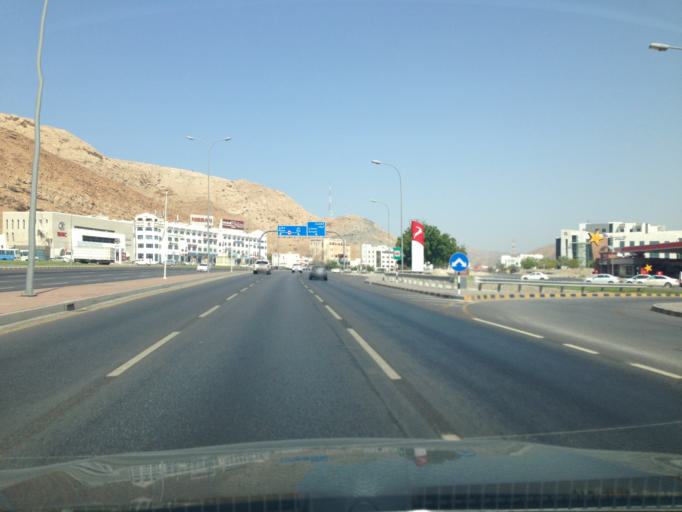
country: OM
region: Muhafazat Masqat
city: Muscat
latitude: 23.6009
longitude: 58.5163
